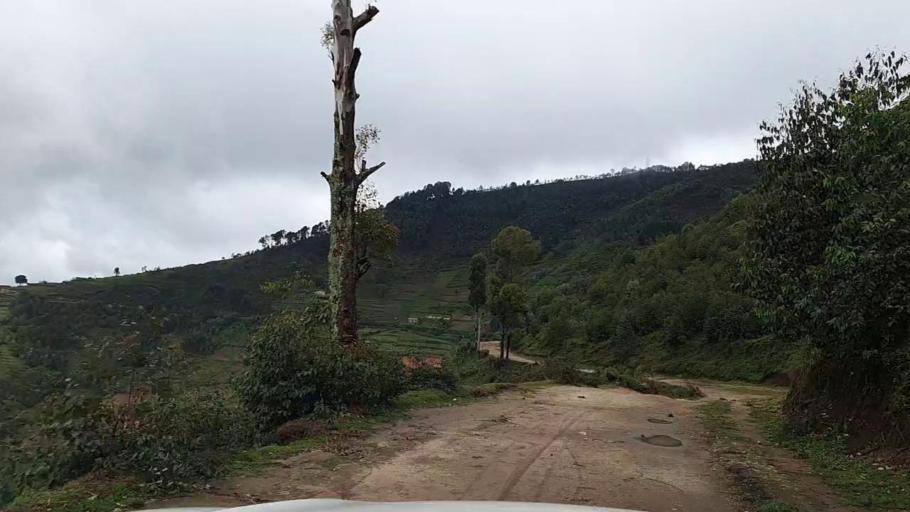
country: RW
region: Southern Province
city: Gikongoro
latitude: -2.3634
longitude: 29.4957
